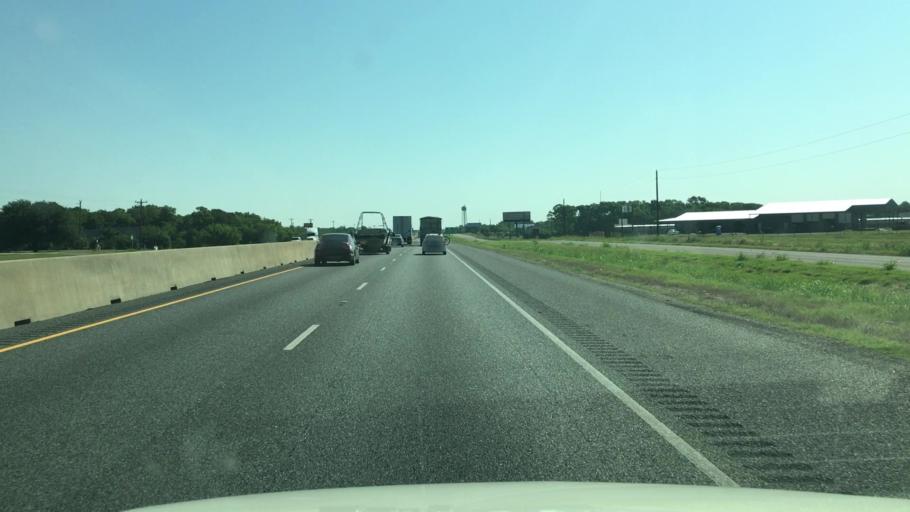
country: US
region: Texas
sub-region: Hunt County
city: Caddo Mills
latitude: 33.0062
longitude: -96.2269
